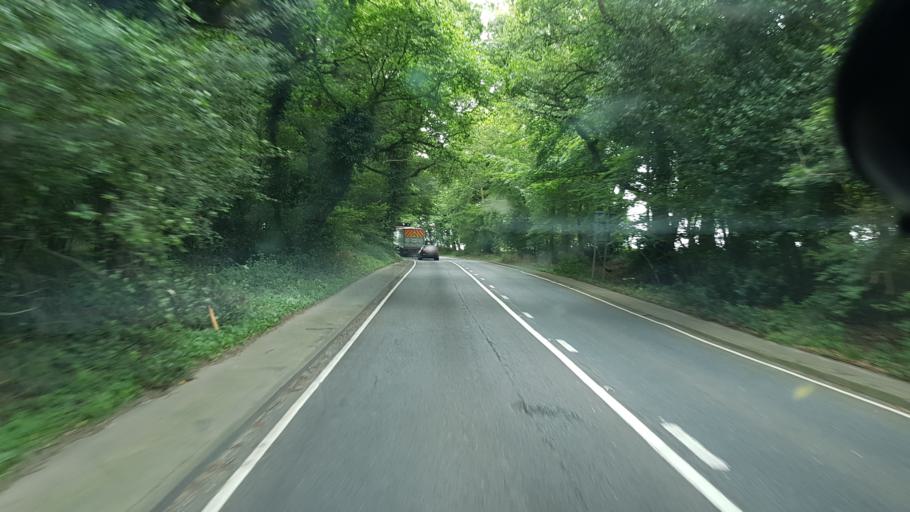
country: GB
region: England
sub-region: Surrey
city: Godstone
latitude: 51.2269
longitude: -0.0471
